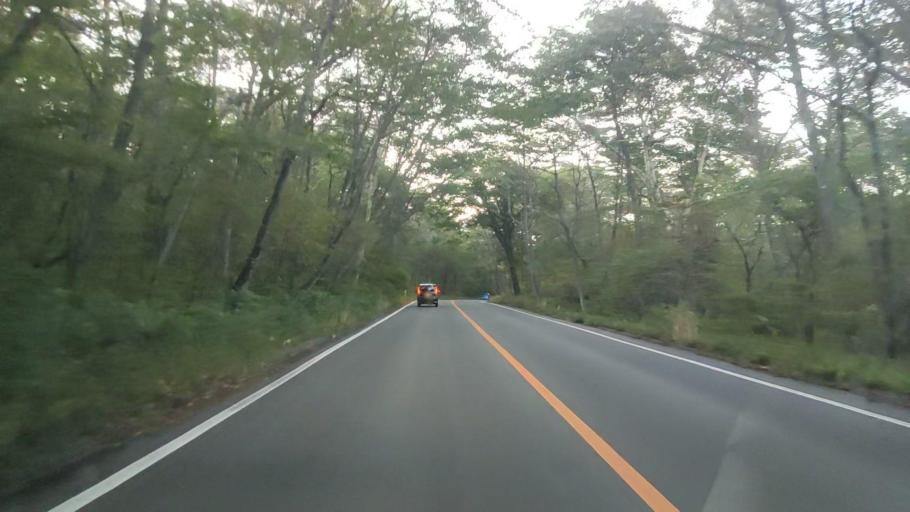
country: JP
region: Nagano
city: Komoro
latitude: 36.4102
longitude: 138.5704
